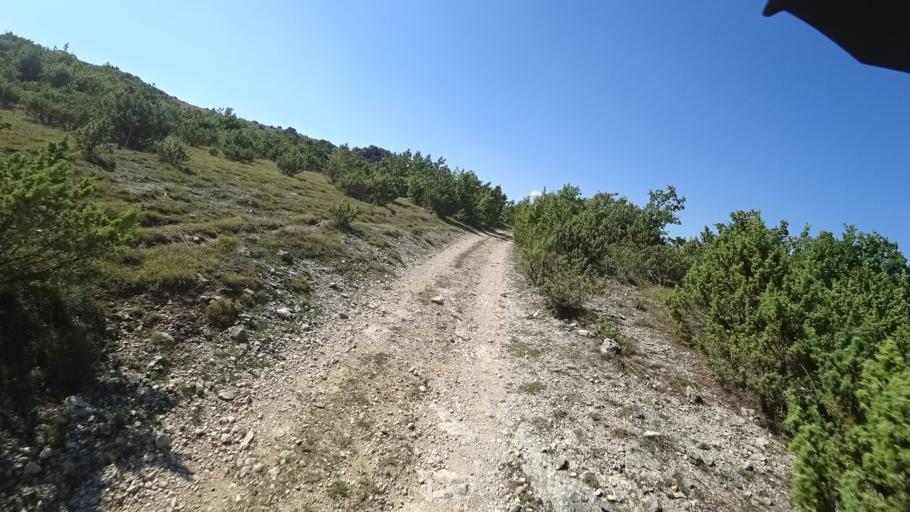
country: HR
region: Splitsko-Dalmatinska
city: Hrvace
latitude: 43.9396
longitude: 16.4576
